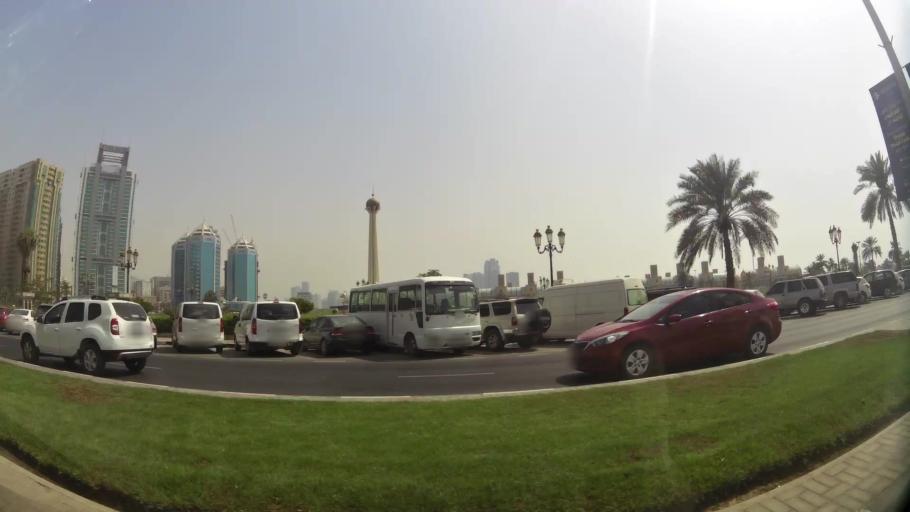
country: AE
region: Ash Shariqah
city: Sharjah
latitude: 25.3488
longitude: 55.3867
